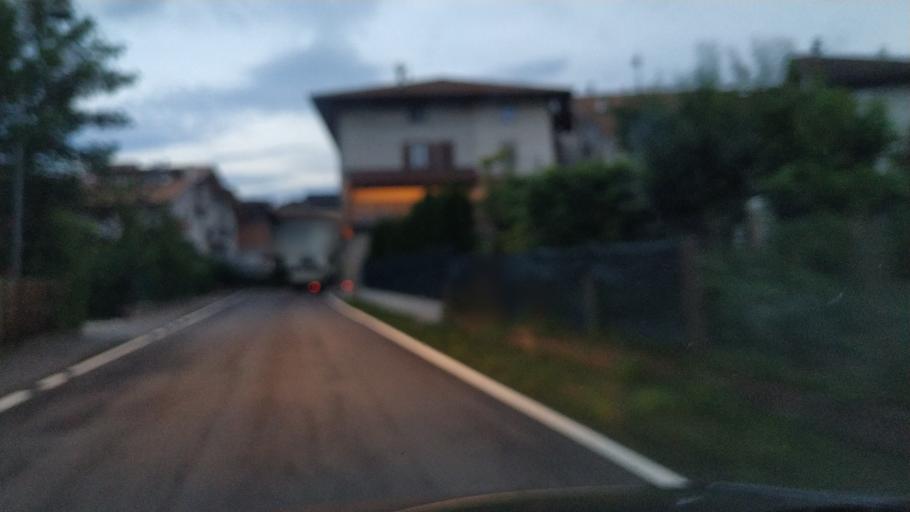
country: IT
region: Trentino-Alto Adige
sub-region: Provincia di Trento
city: Romallo
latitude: 46.3974
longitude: 11.0670
